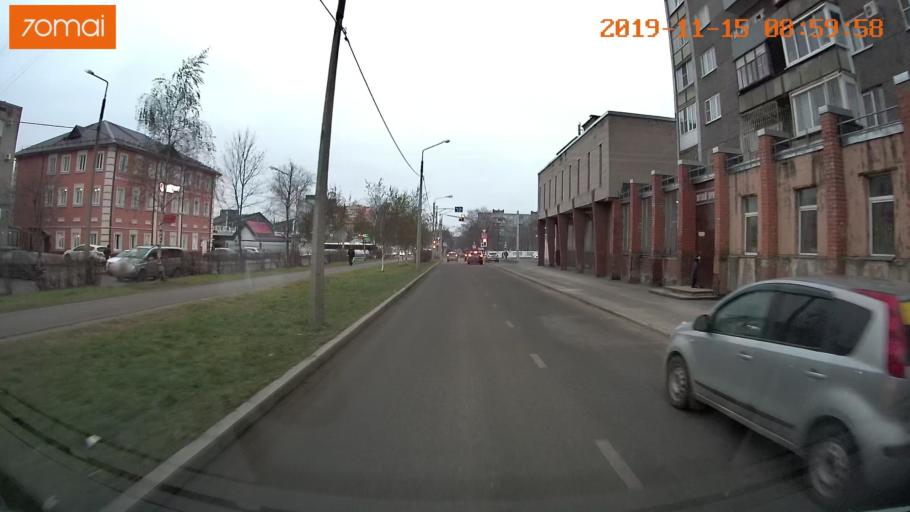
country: RU
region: Vologda
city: Cherepovets
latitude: 59.1293
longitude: 37.9245
